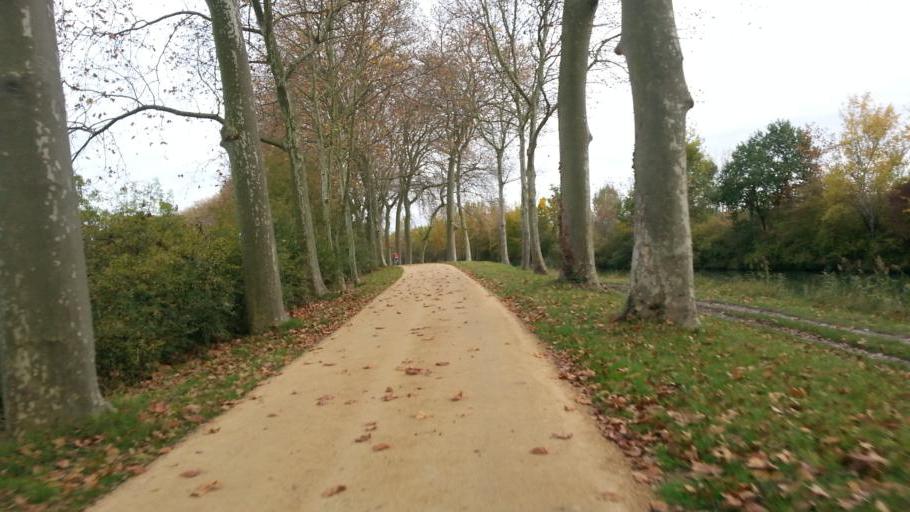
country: FR
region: Midi-Pyrenees
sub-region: Departement de la Haute-Garonne
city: Castanet-Tolosan
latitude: 43.5274
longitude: 1.5094
